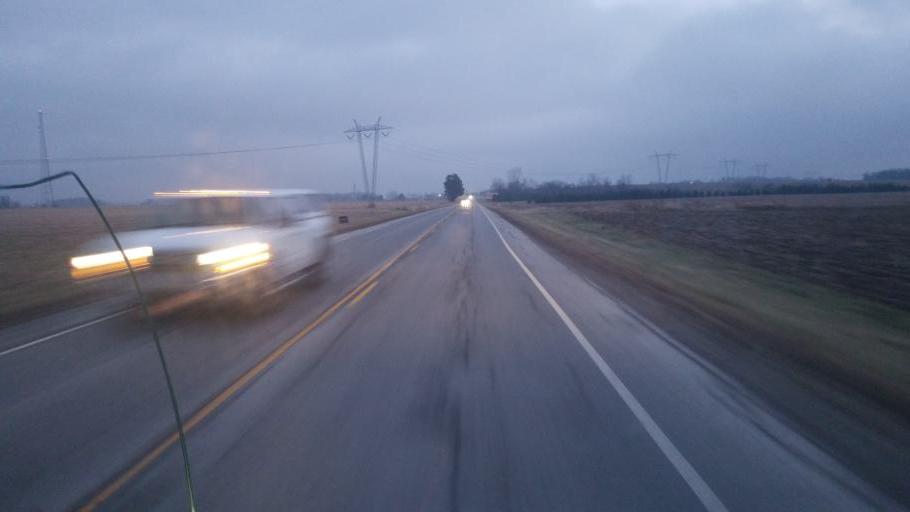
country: US
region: Ohio
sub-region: Crawford County
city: Bucyrus
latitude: 40.8312
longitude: -83.0543
